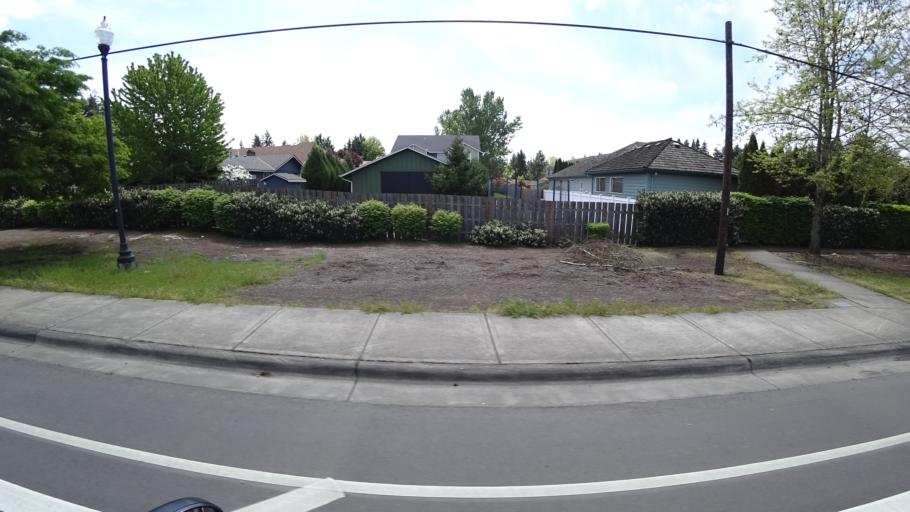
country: US
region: Oregon
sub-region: Washington County
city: Hillsboro
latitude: 45.5499
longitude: -122.9813
